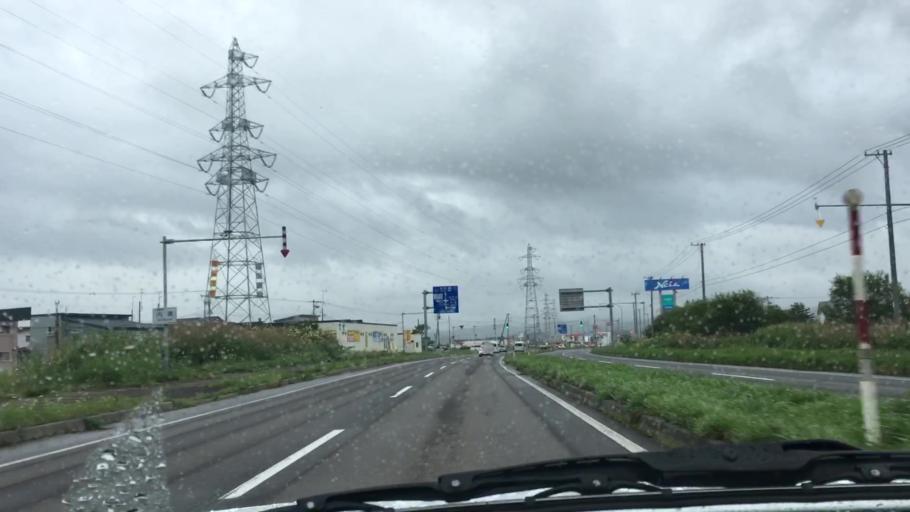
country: JP
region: Hokkaido
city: Nanae
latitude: 42.2552
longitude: 140.2819
